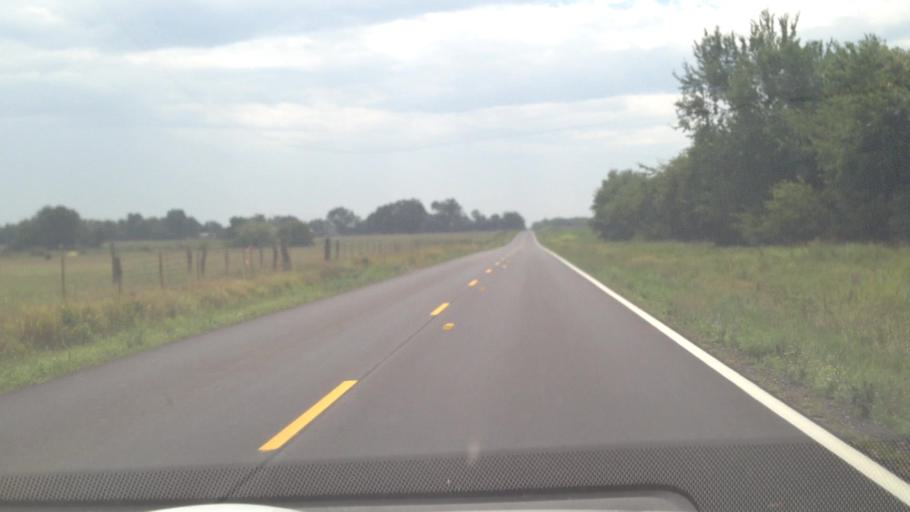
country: US
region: Kansas
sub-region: Crawford County
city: Girard
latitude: 37.5341
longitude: -94.9606
